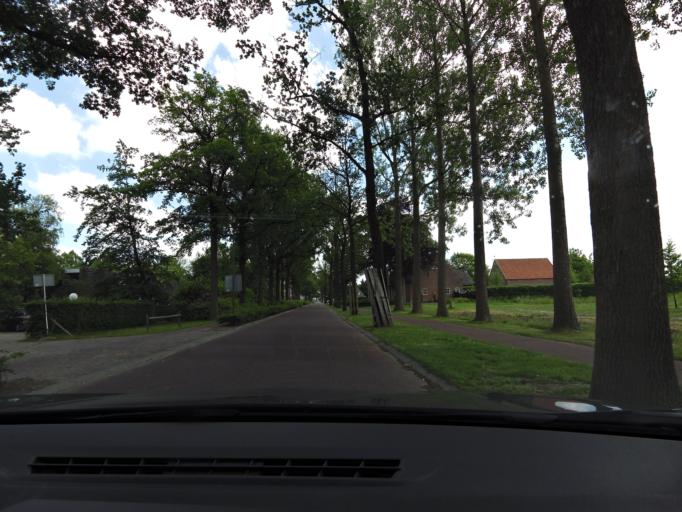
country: NL
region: North Brabant
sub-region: Gemeente Loon op Zand
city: Loon op Zand
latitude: 51.6134
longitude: 5.1352
